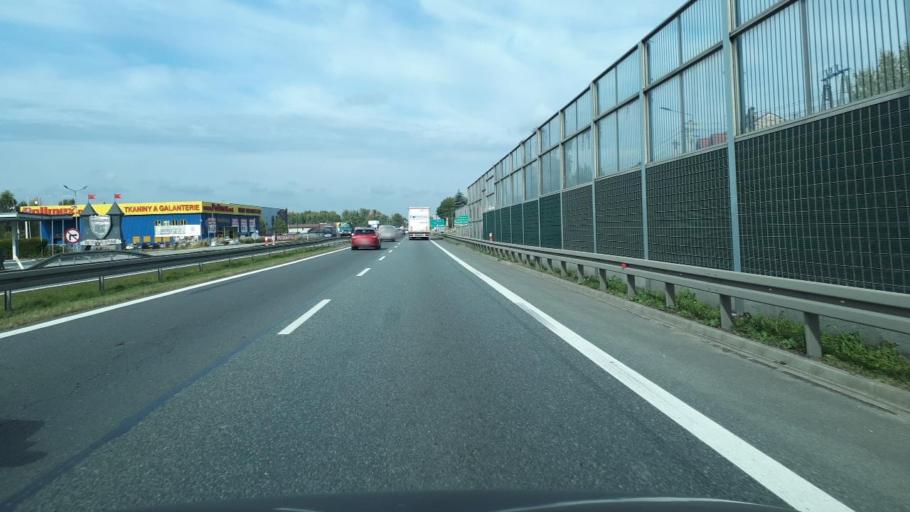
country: PL
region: Silesian Voivodeship
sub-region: Powiat pszczynski
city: Goczalkowice Zdroj
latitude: 49.9599
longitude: 18.9625
